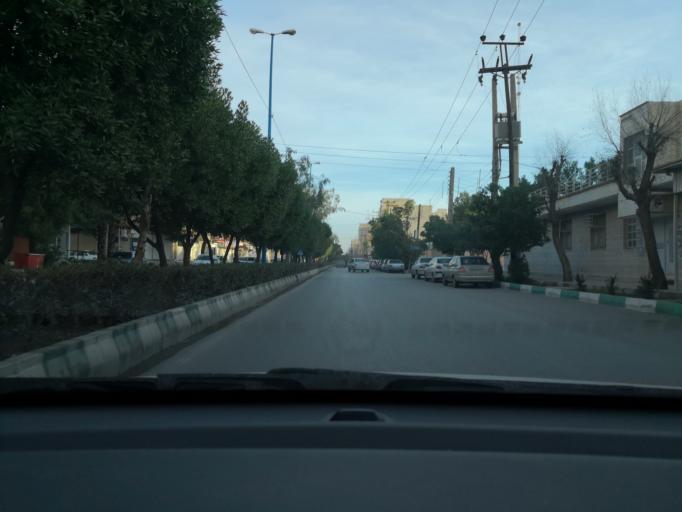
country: IR
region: Khuzestan
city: Ahvaz
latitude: 31.3512
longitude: 48.6769
